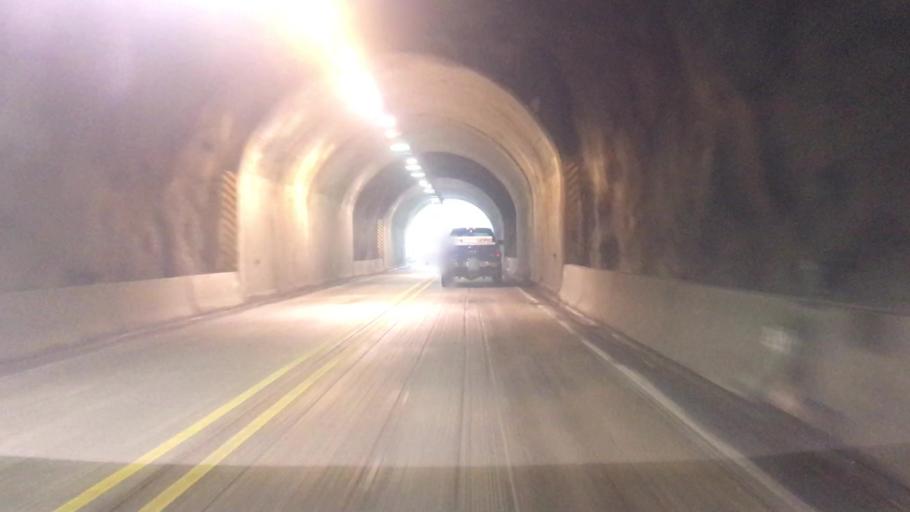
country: US
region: Oregon
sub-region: Lane County
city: Florence
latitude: 44.1316
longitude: -124.1222
